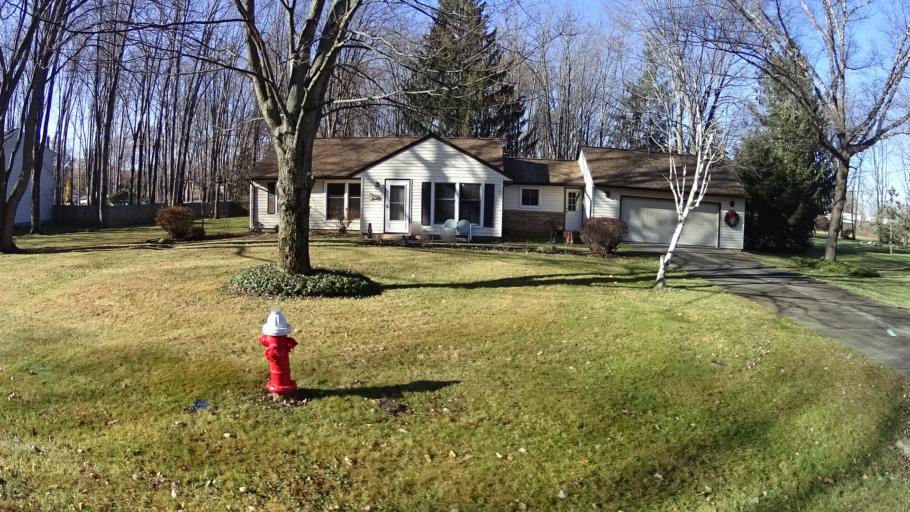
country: US
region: Ohio
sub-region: Lorain County
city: North Ridgeville
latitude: 41.4165
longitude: -81.9931
